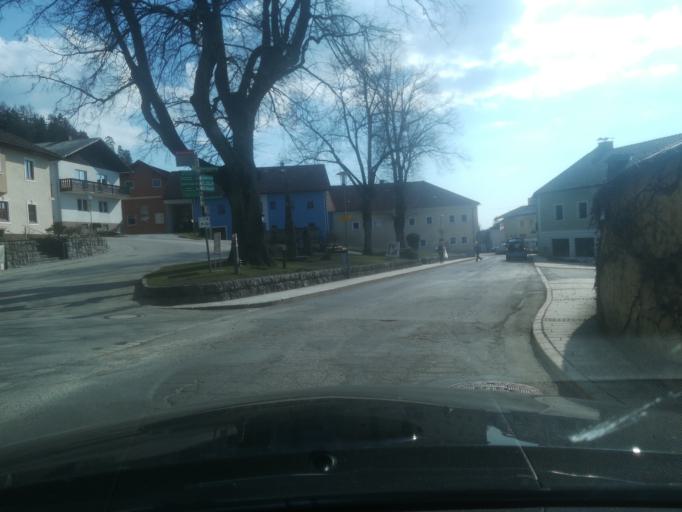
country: AT
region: Upper Austria
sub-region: Politischer Bezirk Freistadt
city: Freistadt
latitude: 48.4436
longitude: 14.6779
